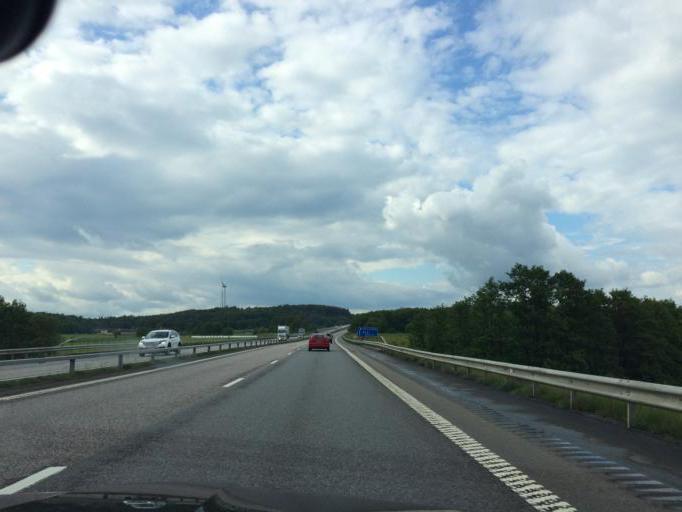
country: SE
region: Halland
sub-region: Kungsbacka Kommun
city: Frillesas
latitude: 57.3207
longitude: 12.2085
